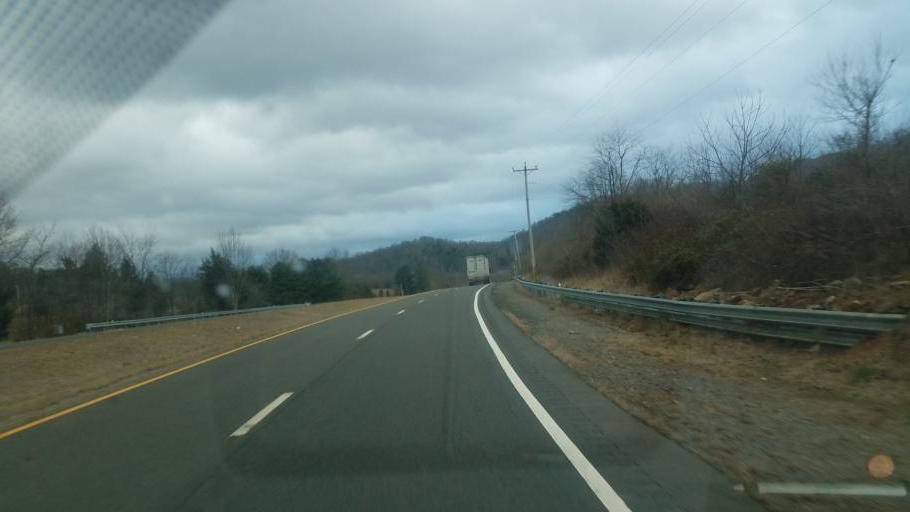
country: US
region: Virginia
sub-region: Giles County
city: Pearisburg
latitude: 37.2641
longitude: -80.7100
